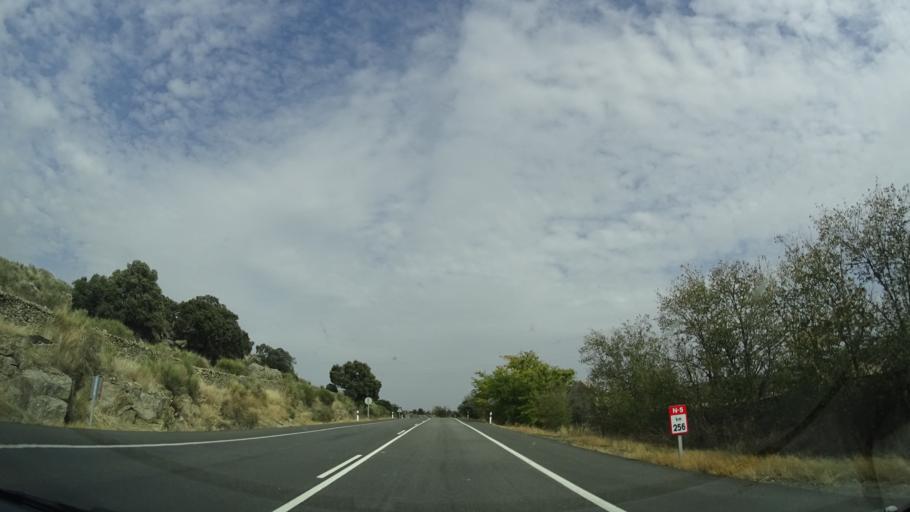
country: ES
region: Extremadura
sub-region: Provincia de Caceres
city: Trujillo
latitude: 39.4393
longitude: -5.8881
